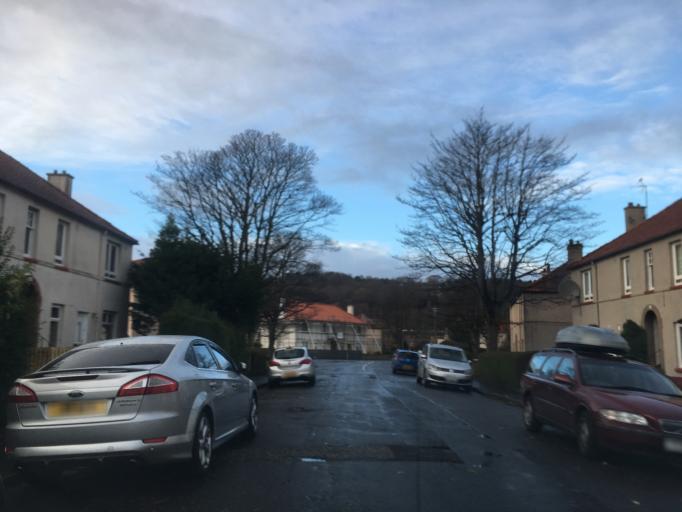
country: GB
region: Scotland
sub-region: Edinburgh
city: Colinton
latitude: 55.9416
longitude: -3.2539
